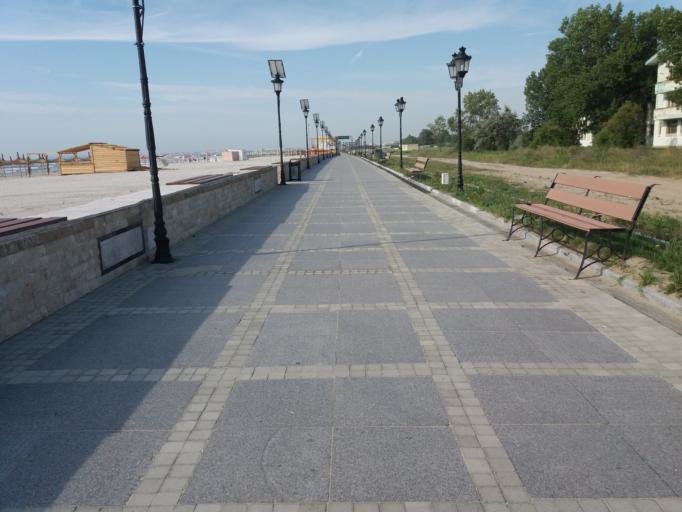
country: RO
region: Constanta
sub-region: Comuna Navodari
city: Navodari
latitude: 44.3172
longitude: 28.6339
